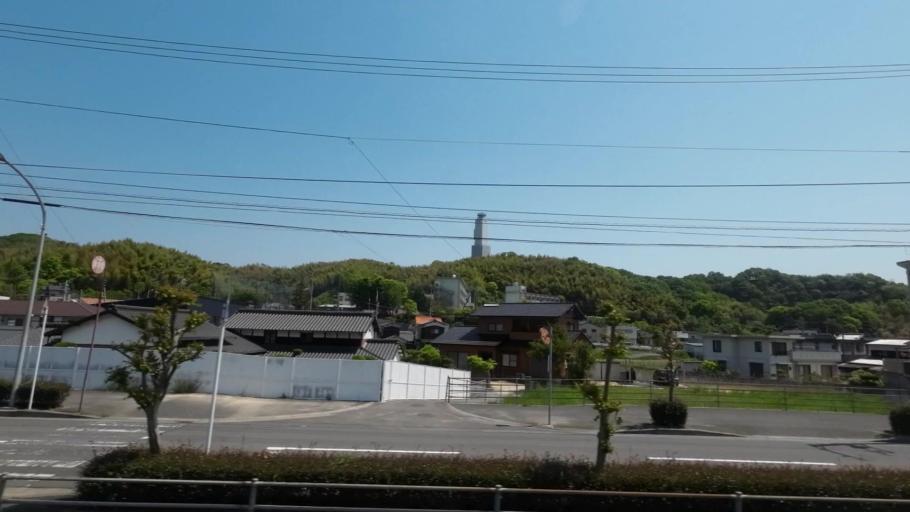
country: JP
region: Ehime
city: Hojo
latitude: 34.0884
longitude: 132.9838
